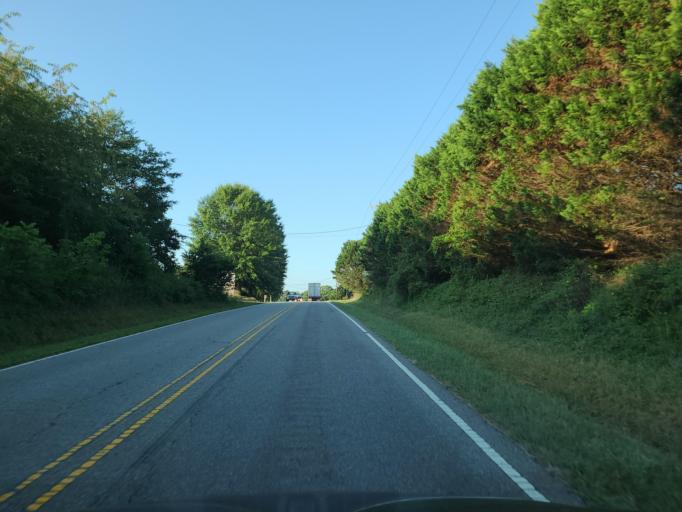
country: US
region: North Carolina
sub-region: Catawba County
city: Mountain View
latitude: 35.6405
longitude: -81.3817
